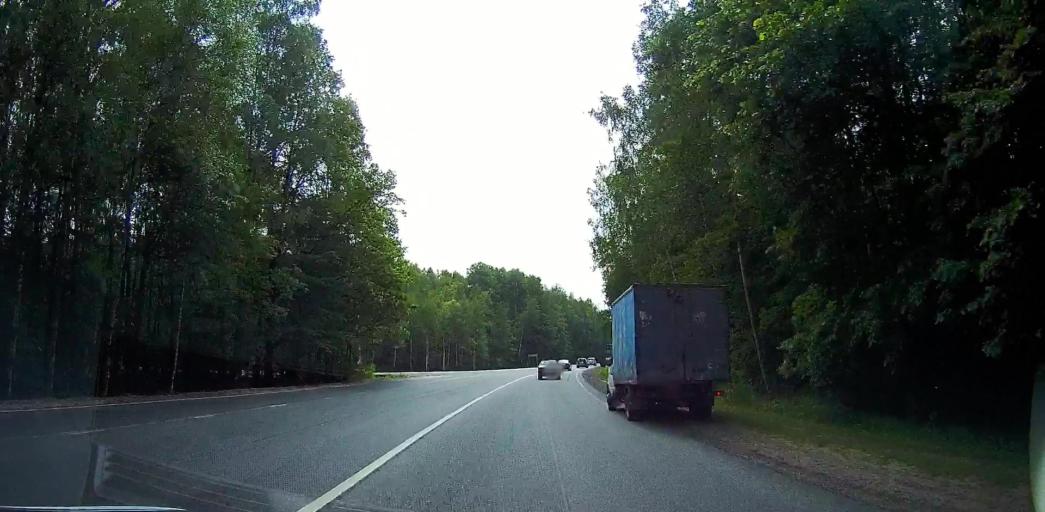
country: RU
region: Moskovskaya
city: Stupino
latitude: 54.9810
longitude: 38.1663
